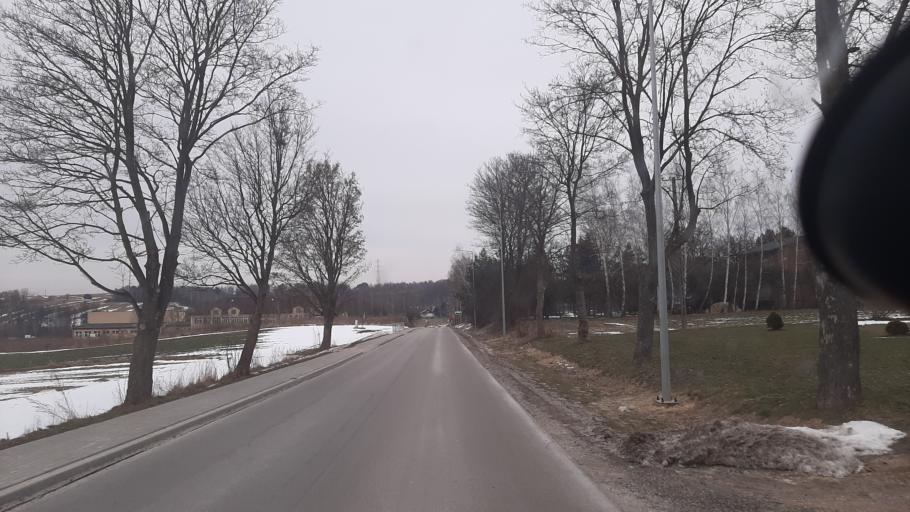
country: PL
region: Lublin Voivodeship
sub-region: Powiat lubelski
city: Jakubowice Murowane
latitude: 51.2975
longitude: 22.6316
